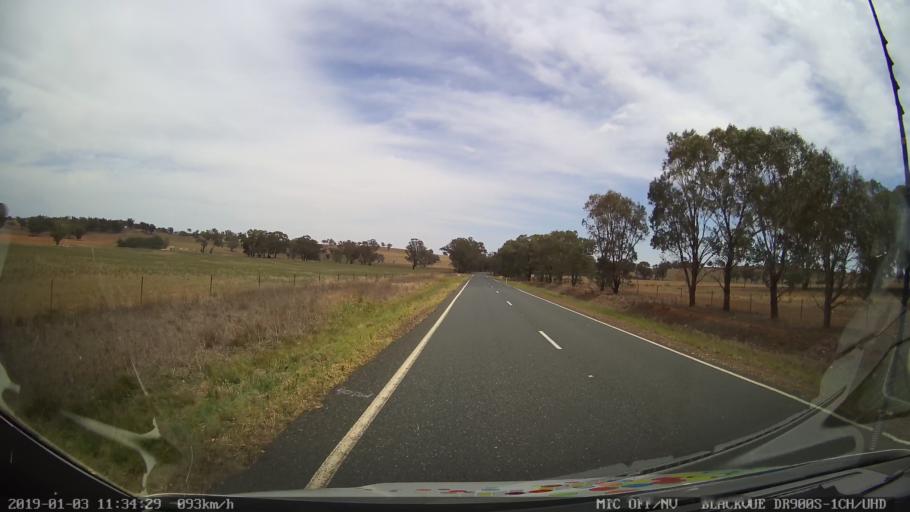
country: AU
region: New South Wales
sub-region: Weddin
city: Grenfell
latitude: -33.9344
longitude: 148.1632
